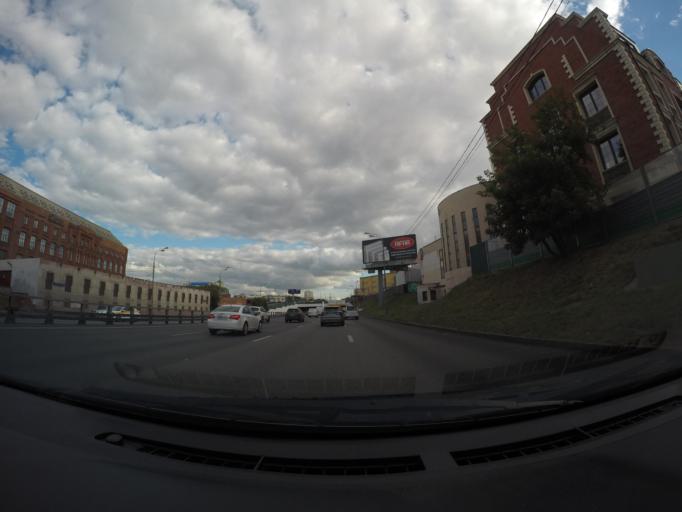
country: RU
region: Moscow
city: Sokol'niki
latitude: 55.7895
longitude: 37.6579
